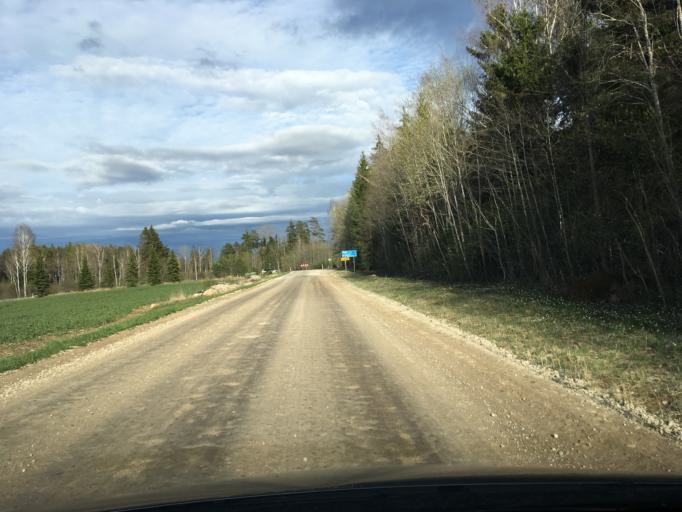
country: EE
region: Raplamaa
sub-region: Maerjamaa vald
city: Marjamaa
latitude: 59.0235
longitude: 24.4464
